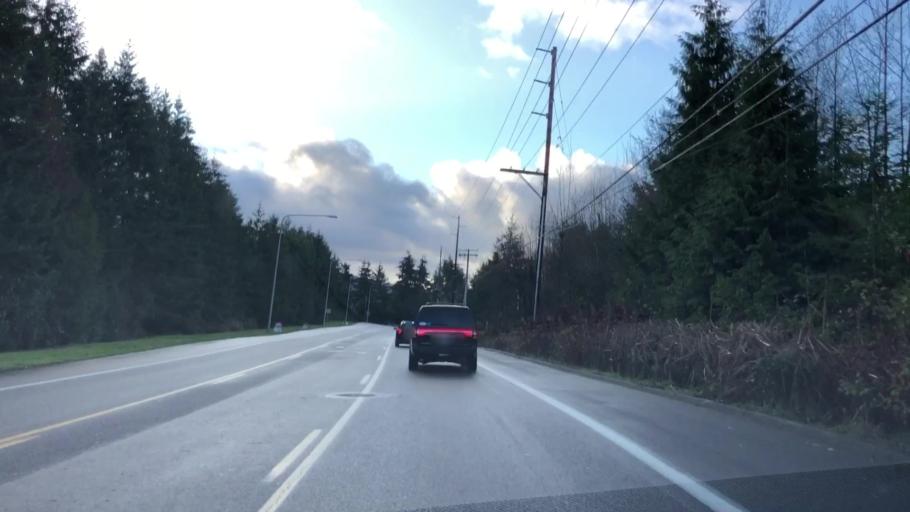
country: US
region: Washington
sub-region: King County
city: Issaquah
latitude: 47.5660
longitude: -122.0254
